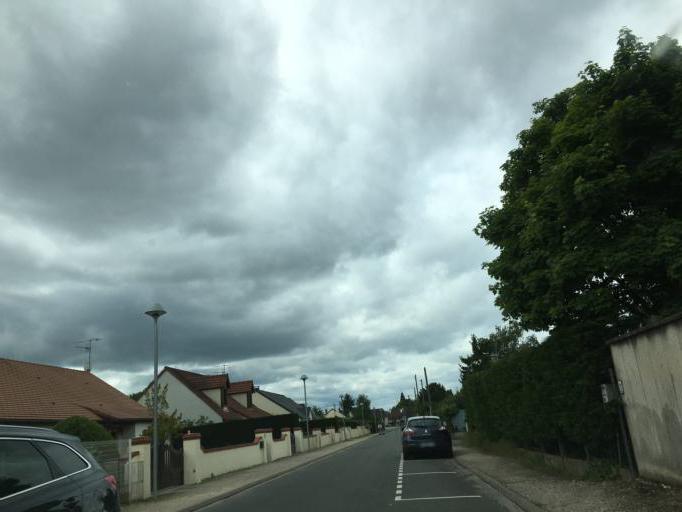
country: FR
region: Centre
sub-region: Departement du Loiret
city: Semoy
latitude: 47.9384
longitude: 1.9439
